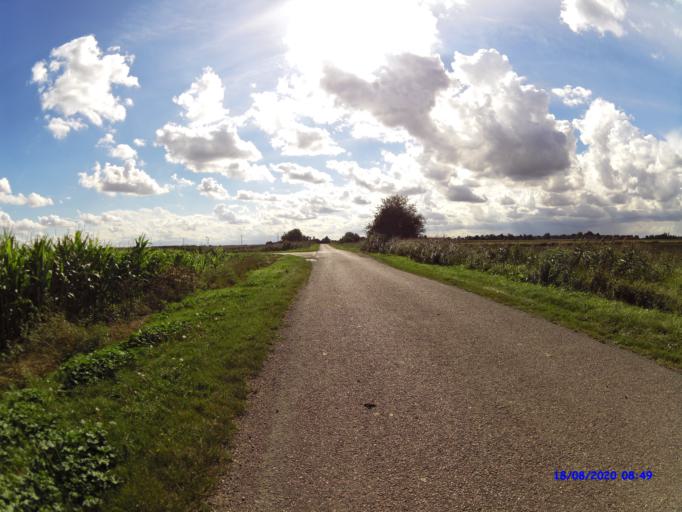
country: GB
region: England
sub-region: Cambridgeshire
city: Ramsey
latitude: 52.4860
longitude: -0.0963
